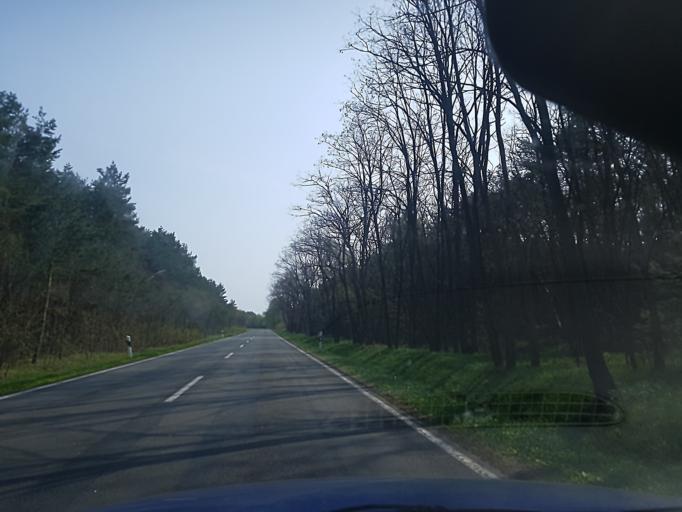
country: DE
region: Saxony
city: Beilrode
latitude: 51.5910
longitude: 13.1086
